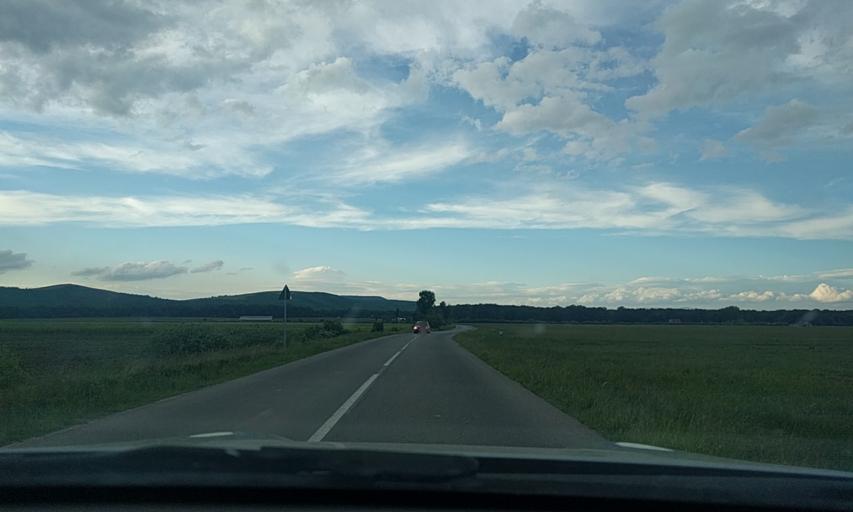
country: RO
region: Brasov
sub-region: Comuna Harman
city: Harman
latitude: 45.7375
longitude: 25.7033
